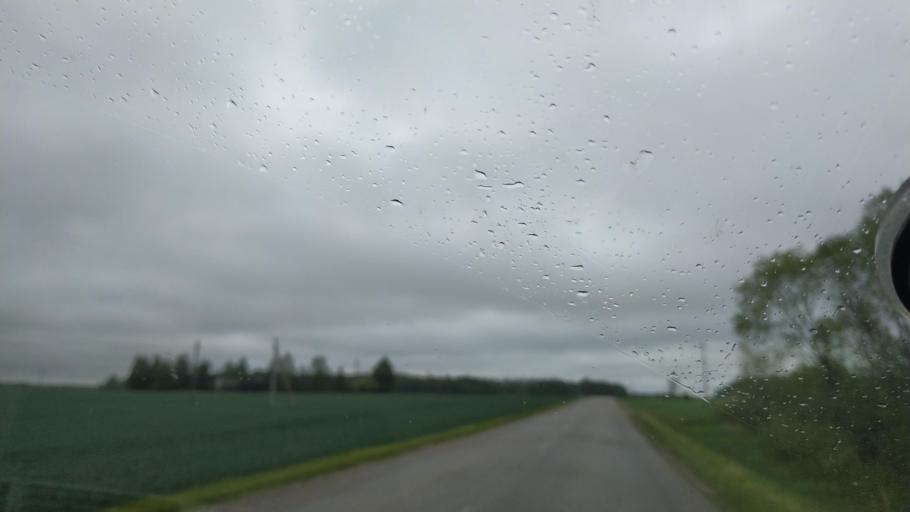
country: LT
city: Vabalninkas
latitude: 56.0028
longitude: 24.6364
